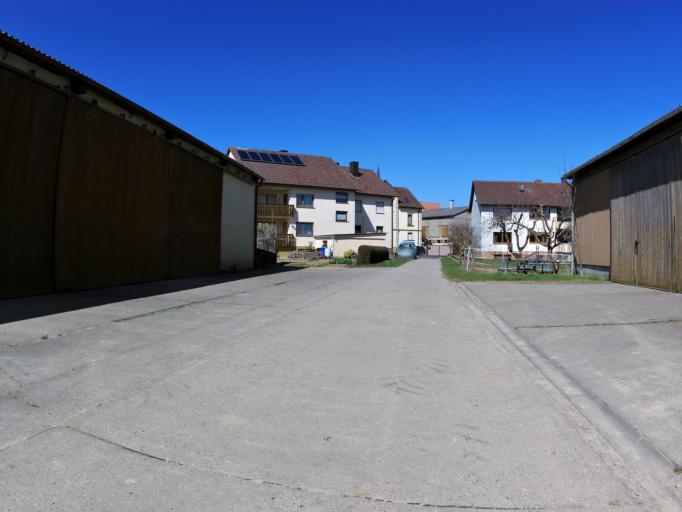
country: DE
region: Bavaria
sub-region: Regierungsbezirk Unterfranken
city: Prosselsheim
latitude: 49.8613
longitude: 10.1279
